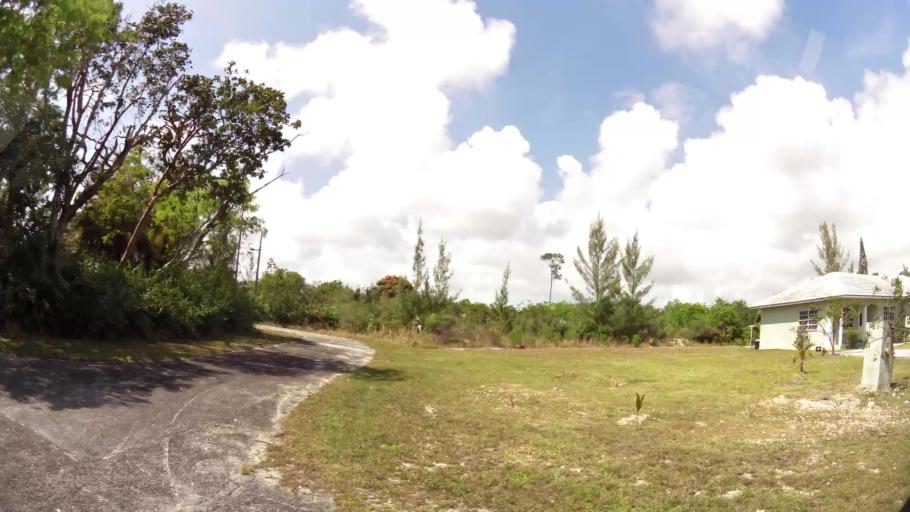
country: BS
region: Freeport
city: Freeport
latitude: 26.5069
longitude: -78.7120
